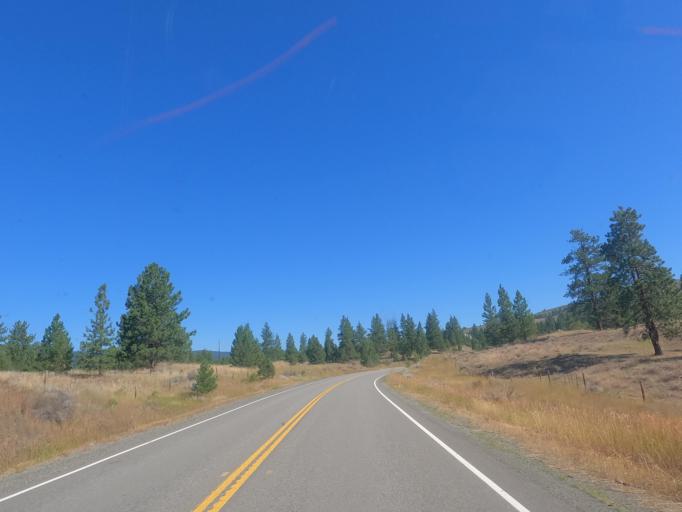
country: CA
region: British Columbia
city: Merritt
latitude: 50.1804
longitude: -120.8556
